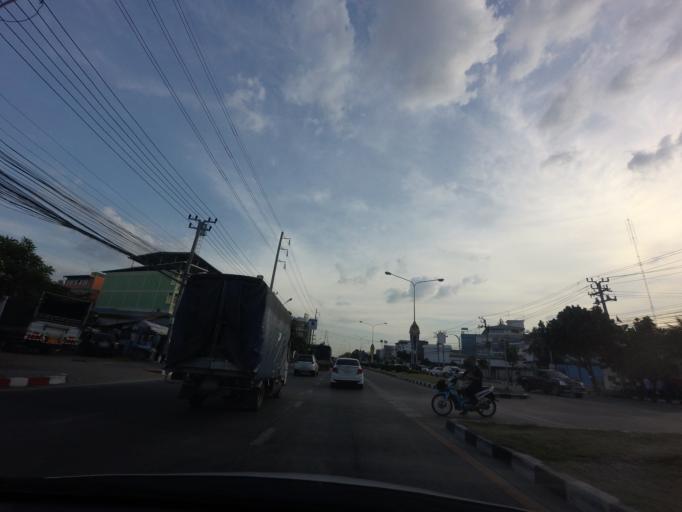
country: TH
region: Bangkok
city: Bang Khun Thian
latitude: 13.6349
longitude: 100.4333
